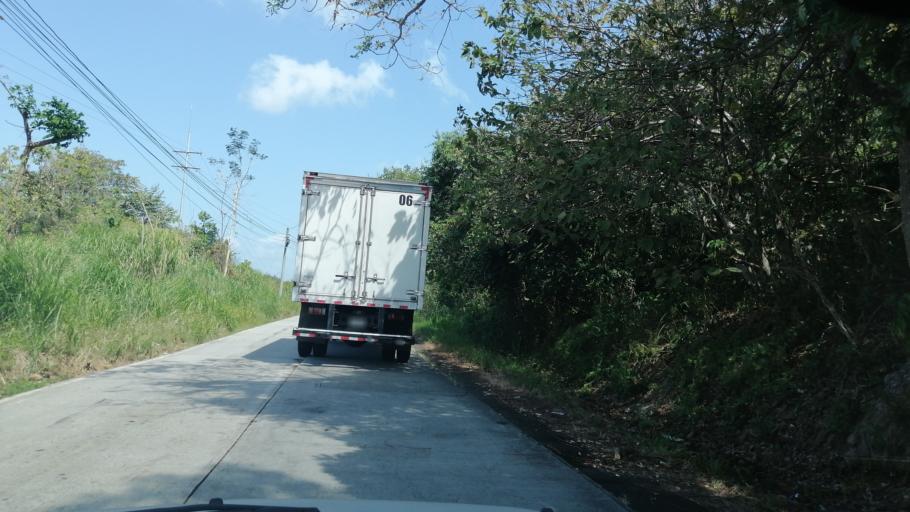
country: PA
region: Panama
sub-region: Distrito de Panama
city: Ancon
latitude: 8.9383
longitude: -79.5742
